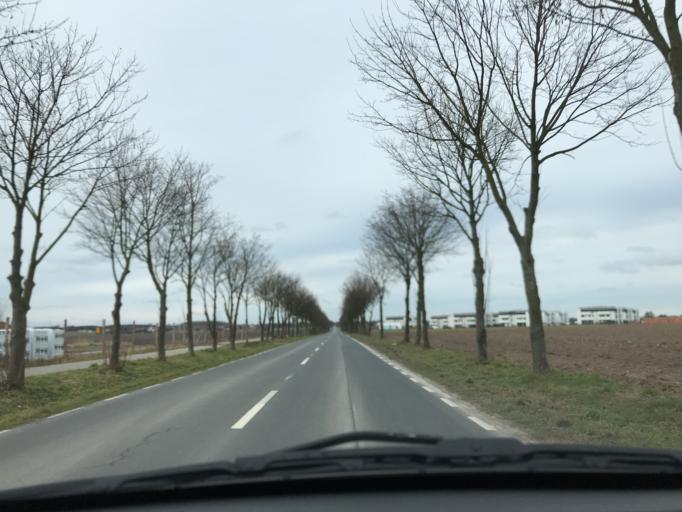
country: PL
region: Greater Poland Voivodeship
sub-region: Powiat poznanski
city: Baranowo
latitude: 52.3925
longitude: 16.7717
